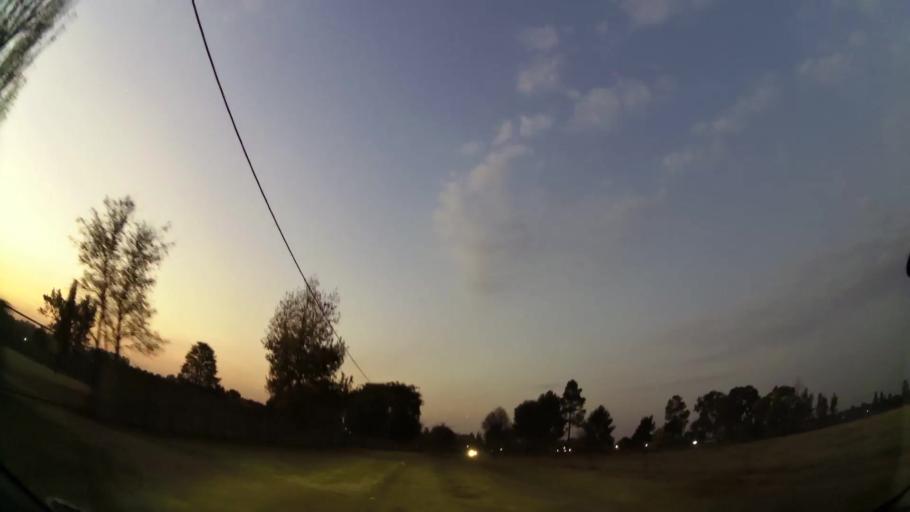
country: ZA
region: Gauteng
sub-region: Ekurhuleni Metropolitan Municipality
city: Benoni
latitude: -26.1116
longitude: 28.3136
